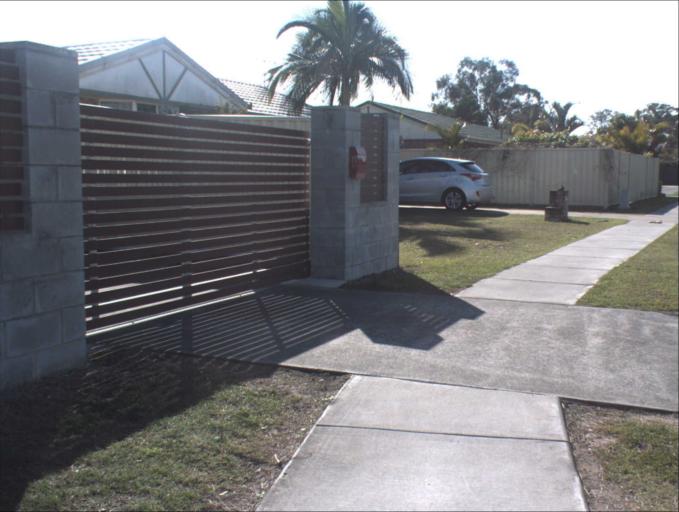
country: AU
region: Queensland
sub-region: Logan
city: Logan City
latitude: -27.6688
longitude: 153.1004
